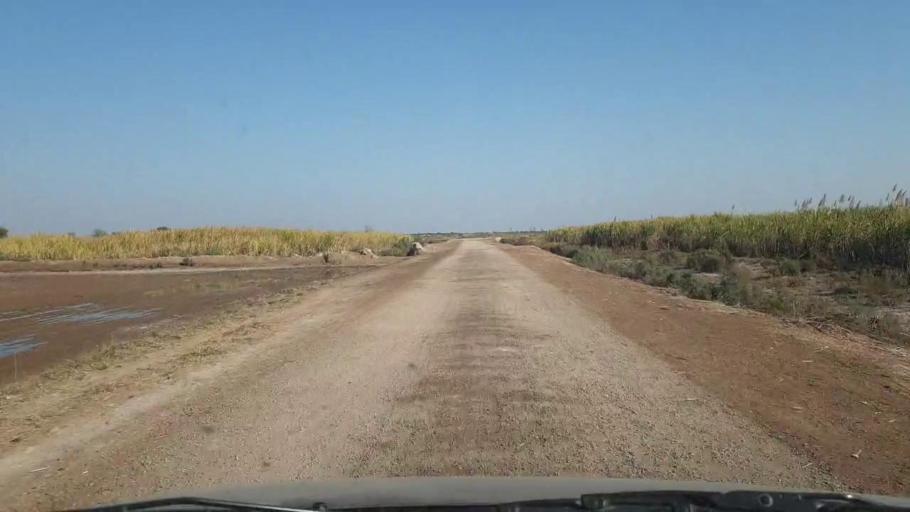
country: PK
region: Sindh
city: Samaro
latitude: 25.3474
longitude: 69.3228
